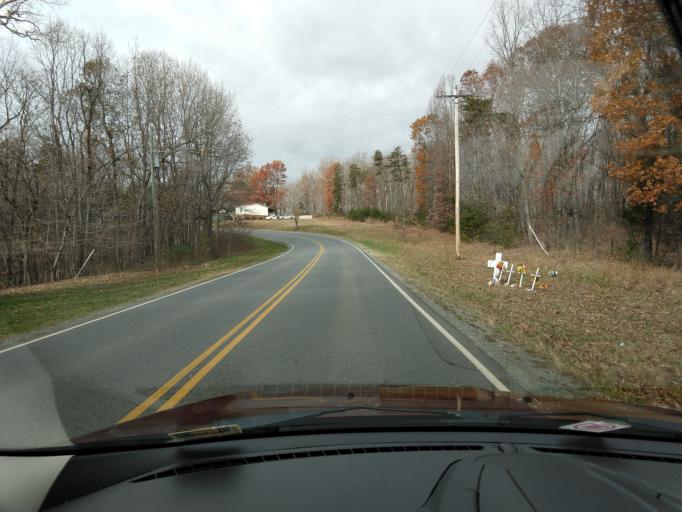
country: US
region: Virginia
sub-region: Franklin County
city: North Shore
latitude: 37.1942
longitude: -79.6822
